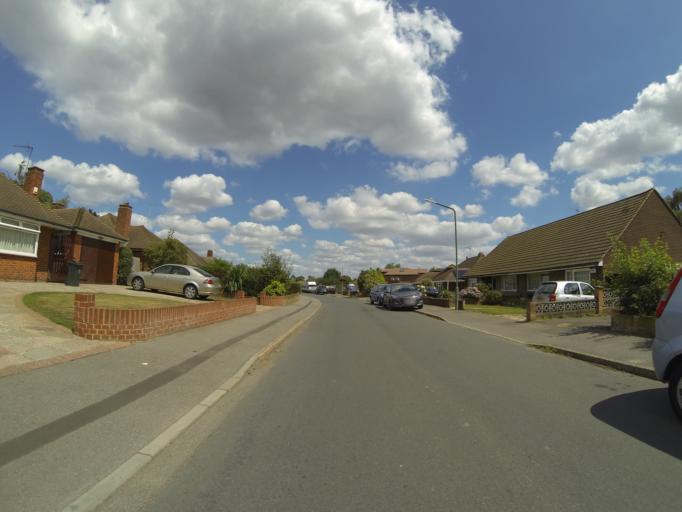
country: GB
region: England
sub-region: Kent
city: Swanley
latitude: 51.4241
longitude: 0.1720
